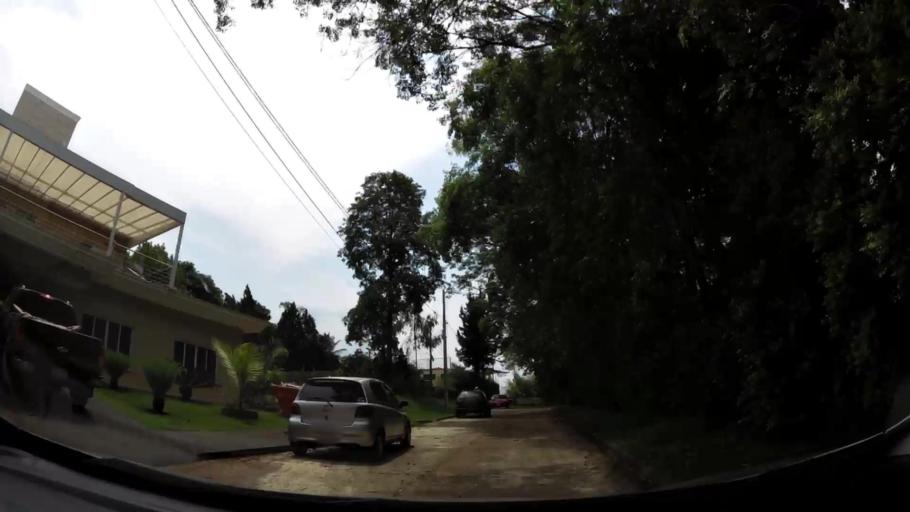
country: PY
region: Alto Parana
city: Ciudad del Este
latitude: -25.4900
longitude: -54.6083
